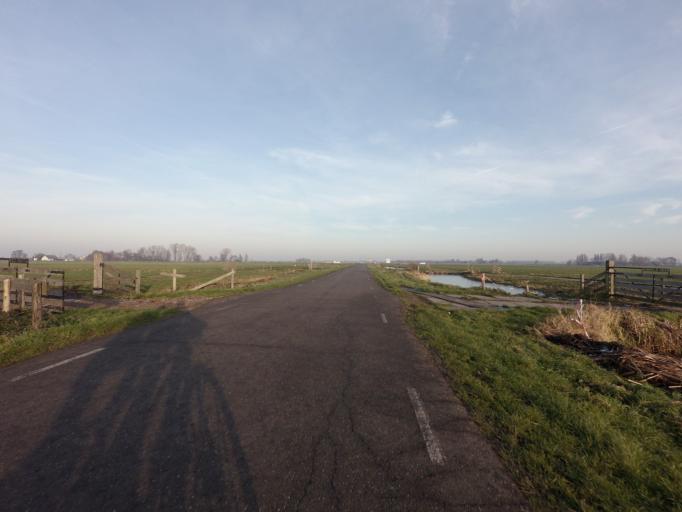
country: NL
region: Utrecht
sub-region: Stichtse Vecht
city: Breukelen
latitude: 52.1827
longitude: 4.9304
